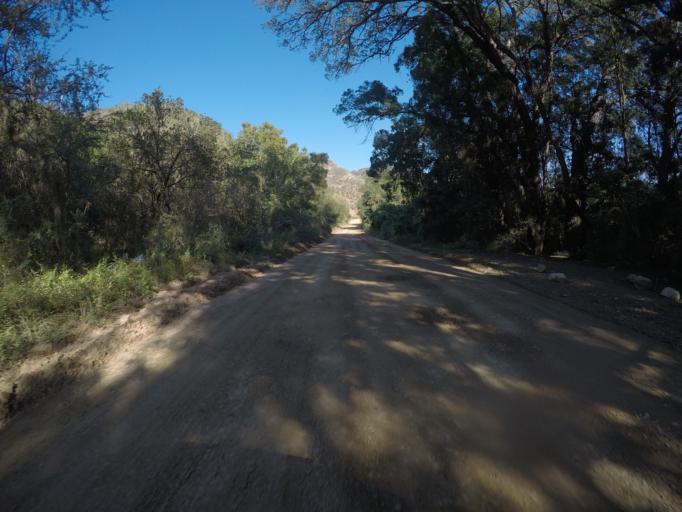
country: ZA
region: Eastern Cape
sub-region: Cacadu District Municipality
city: Kareedouw
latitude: -33.6640
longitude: 24.5466
